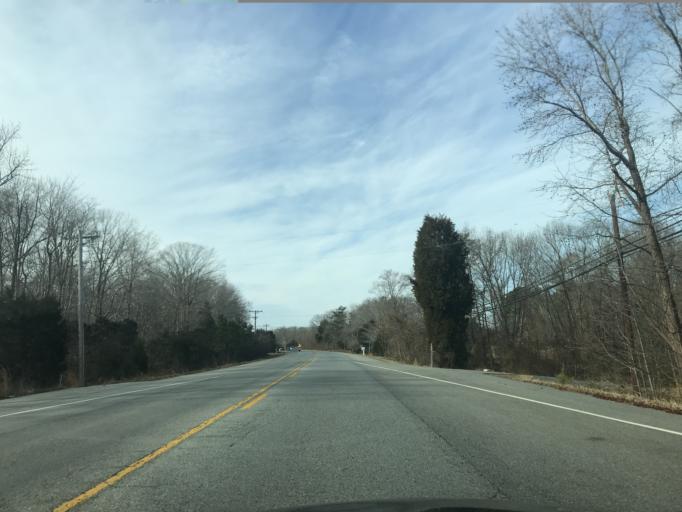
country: US
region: Maryland
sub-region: Charles County
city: La Plata
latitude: 38.5091
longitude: -77.0396
